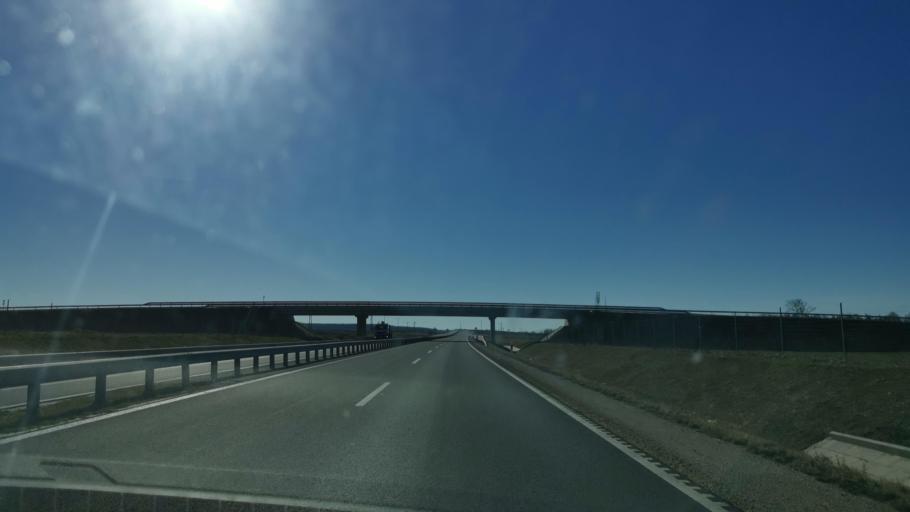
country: HU
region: Somogy
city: Balatonbereny
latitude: 46.6766
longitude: 17.2961
